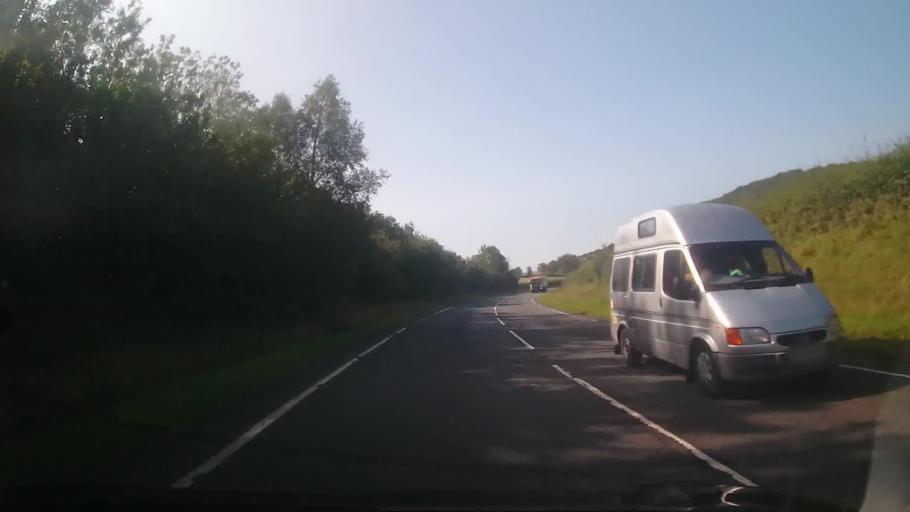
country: GB
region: Wales
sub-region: Sir Powys
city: Rhayader
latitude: 52.1477
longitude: -3.5837
